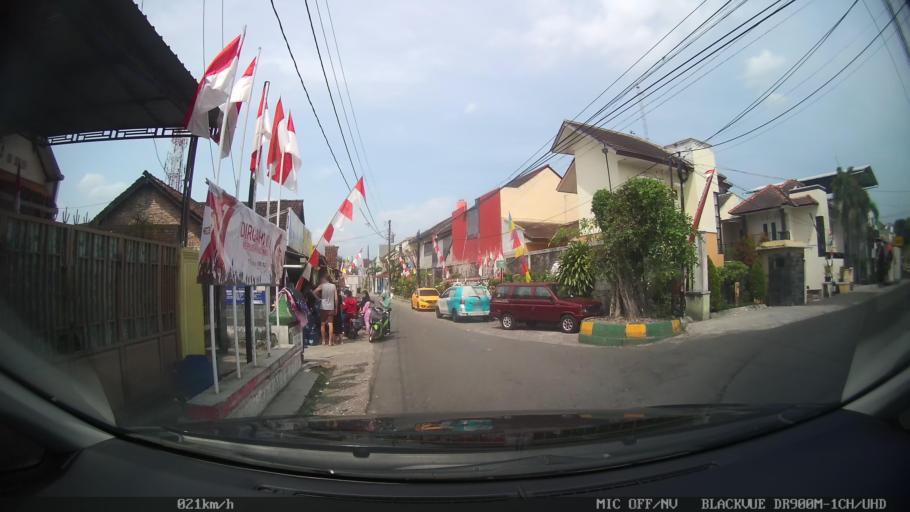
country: ID
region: Daerah Istimewa Yogyakarta
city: Yogyakarta
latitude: -7.7964
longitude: 110.4025
